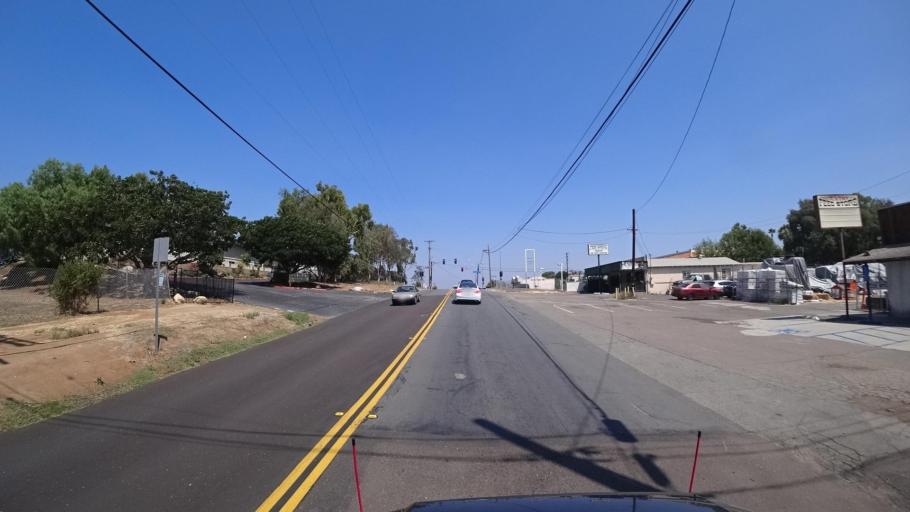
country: US
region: California
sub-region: San Diego County
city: Vista
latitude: 33.2323
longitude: -117.2262
